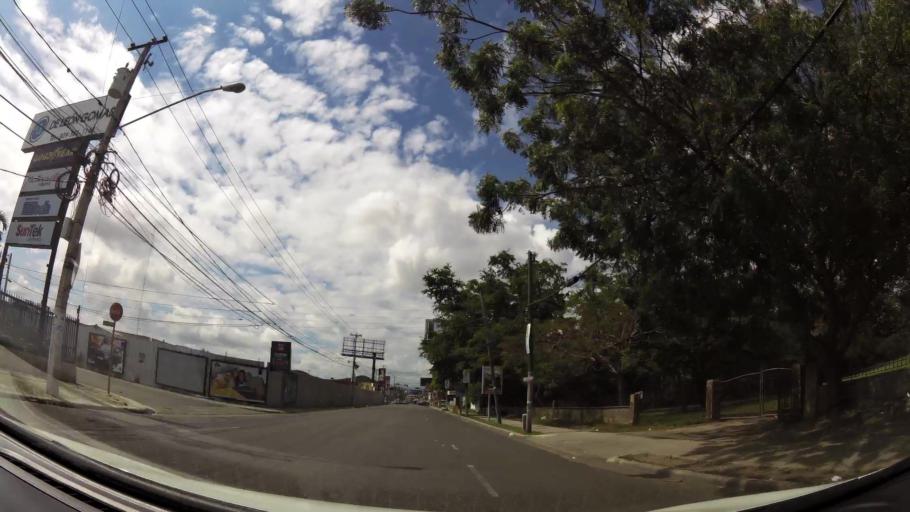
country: DO
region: Santiago
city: Santiago de los Caballeros
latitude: 19.4605
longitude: -70.6995
